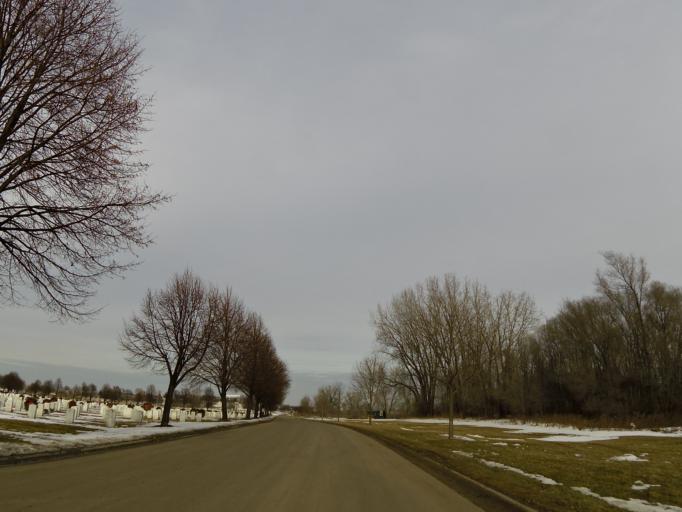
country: US
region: Minnesota
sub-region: Hennepin County
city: Richfield
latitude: 44.8689
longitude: -93.2138
